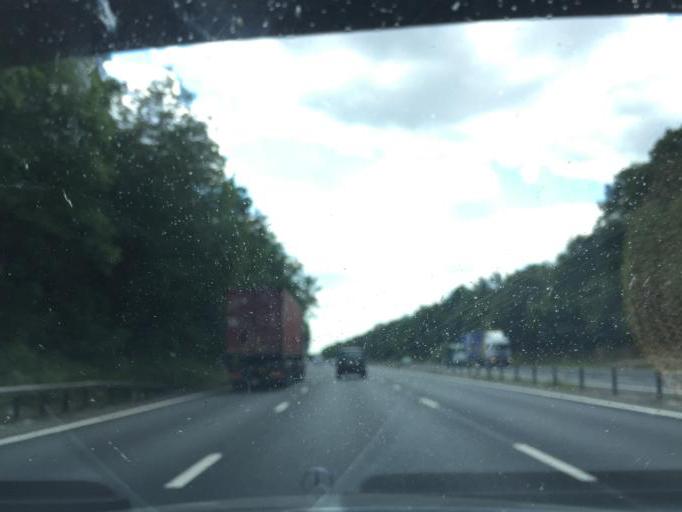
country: GB
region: England
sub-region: Warwickshire
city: Kenilworth
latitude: 52.3404
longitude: -1.5503
